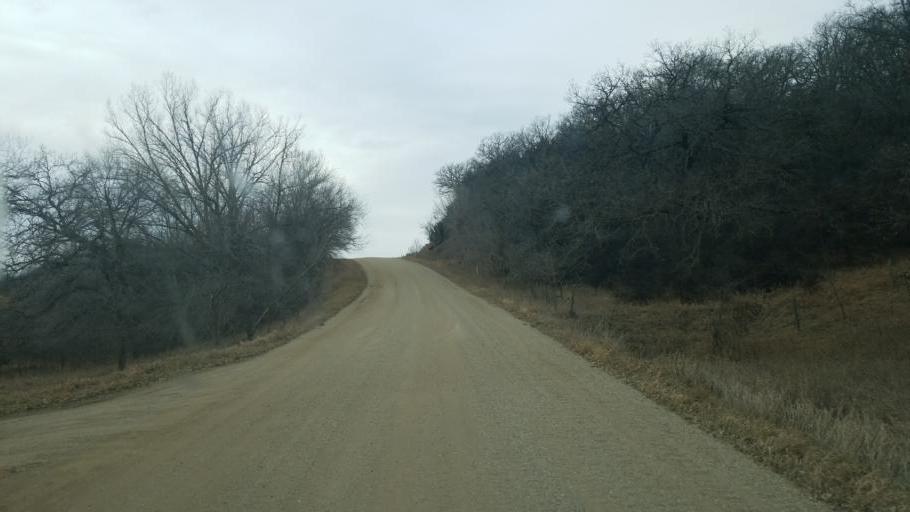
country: US
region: Nebraska
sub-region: Knox County
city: Center
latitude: 42.6109
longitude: -97.8617
